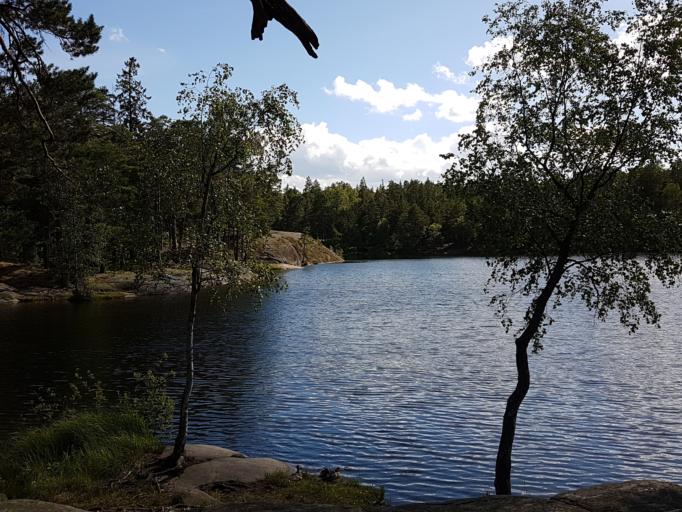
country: SE
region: Stockholm
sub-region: Nacka Kommun
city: Kummelnas
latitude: 59.3417
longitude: 18.2540
